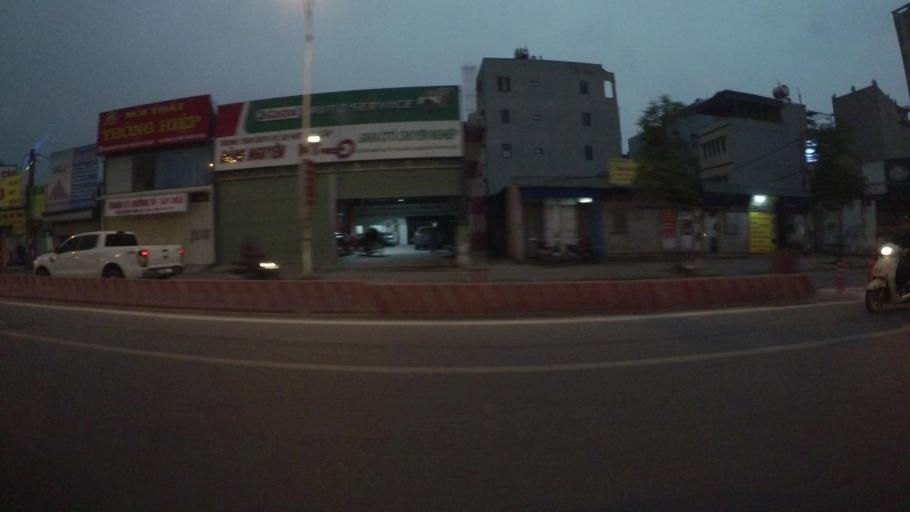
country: VN
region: Ha Noi
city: Trau Quy
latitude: 21.0248
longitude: 105.8949
